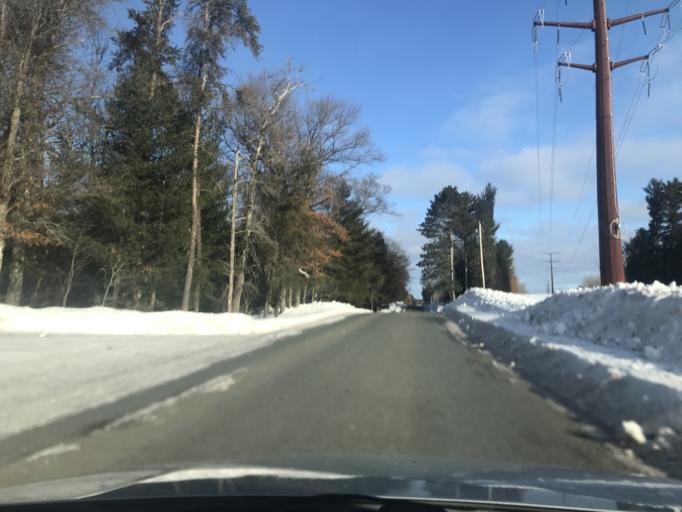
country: US
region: Wisconsin
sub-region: Marinette County
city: Niagara
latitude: 45.6033
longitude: -87.9769
